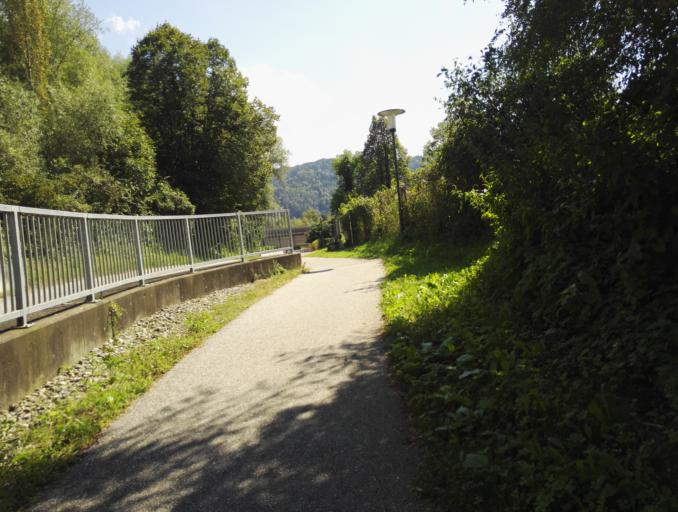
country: AT
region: Styria
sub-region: Politischer Bezirk Graz-Umgebung
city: Peggau
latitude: 47.2013
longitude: 15.3426
